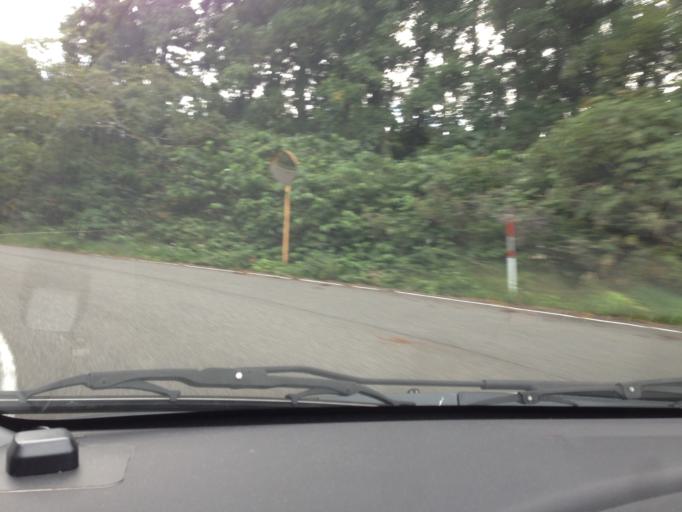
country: JP
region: Fukushima
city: Kitakata
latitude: 37.4572
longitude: 139.7183
